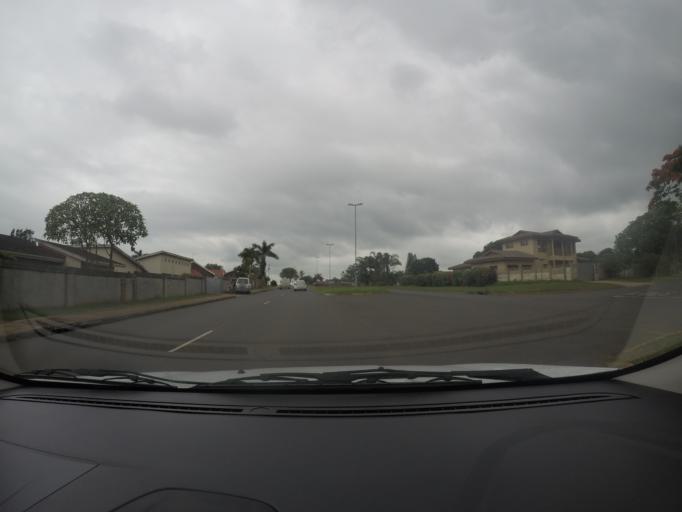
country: ZA
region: KwaZulu-Natal
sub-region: uThungulu District Municipality
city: Empangeni
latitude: -28.7633
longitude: 31.8961
